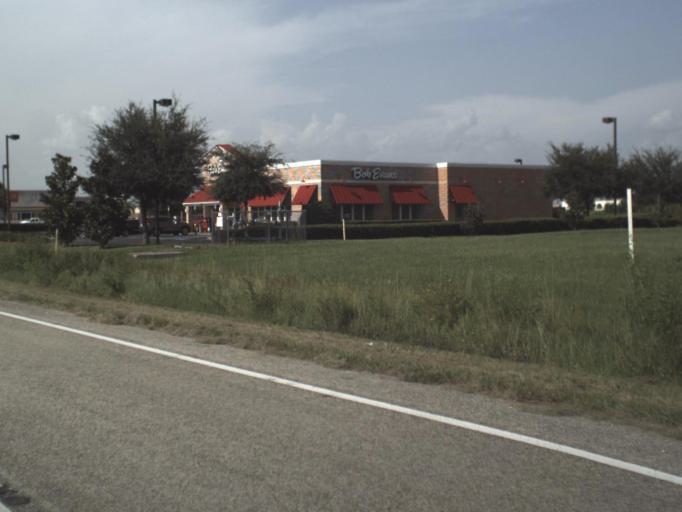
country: US
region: Florida
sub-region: Polk County
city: Lake Wales
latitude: 27.9486
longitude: -81.6173
